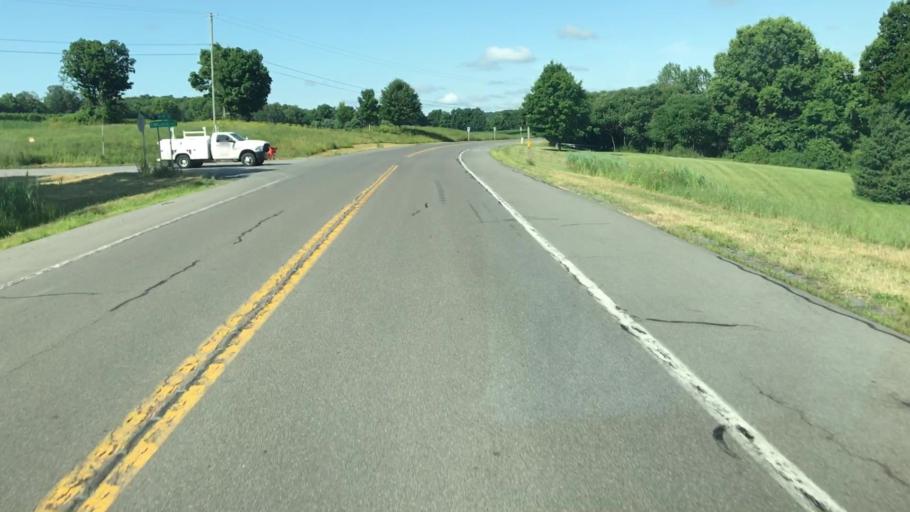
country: US
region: New York
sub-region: Onondaga County
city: Marcellus
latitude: 43.0193
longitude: -76.3747
